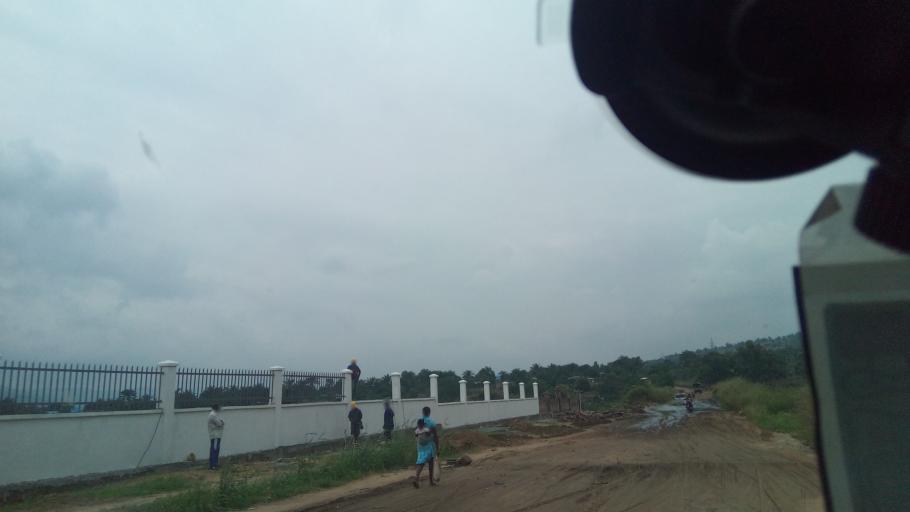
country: CG
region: Brazzaville
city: Brazzaville
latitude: -4.0776
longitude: 15.5428
